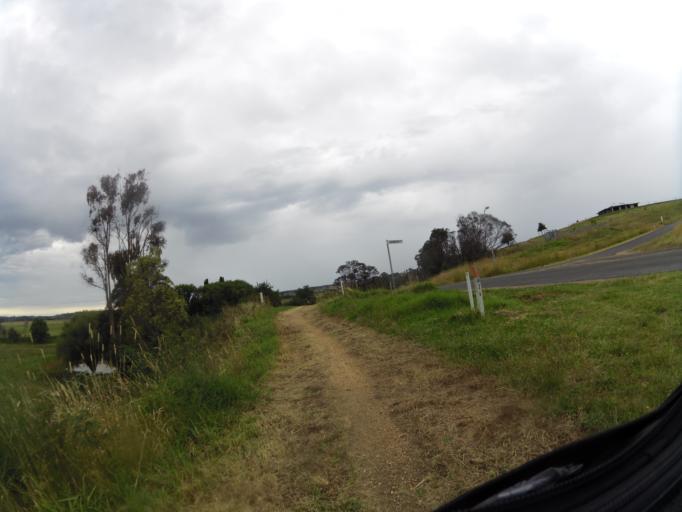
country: AU
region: Victoria
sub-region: East Gippsland
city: Bairnsdale
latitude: -37.7088
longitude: 147.8146
